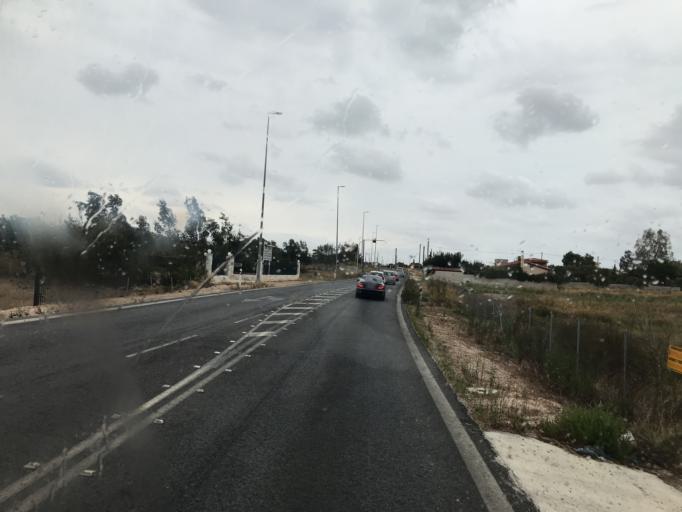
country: GR
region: Attica
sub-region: Nomarchia Anatolikis Attikis
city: Kalyvia Thorikou
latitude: 37.8291
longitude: 23.9058
